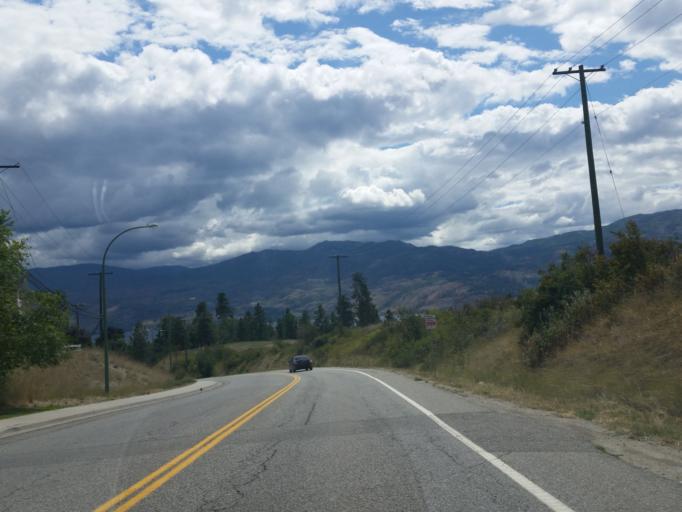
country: CA
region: British Columbia
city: West Kelowna
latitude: 49.8285
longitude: -119.6203
